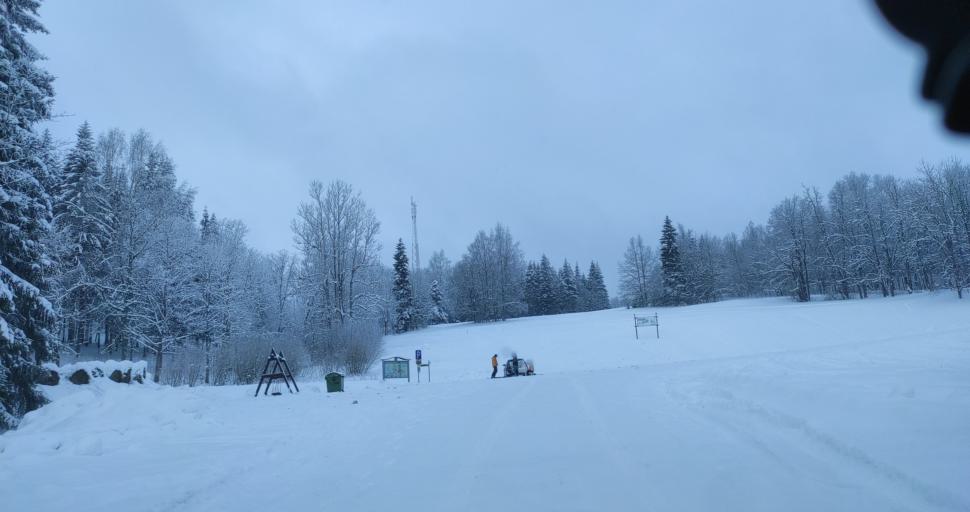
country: LV
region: Vecpiebalga
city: Vecpiebalga
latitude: 56.8713
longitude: 25.9647
